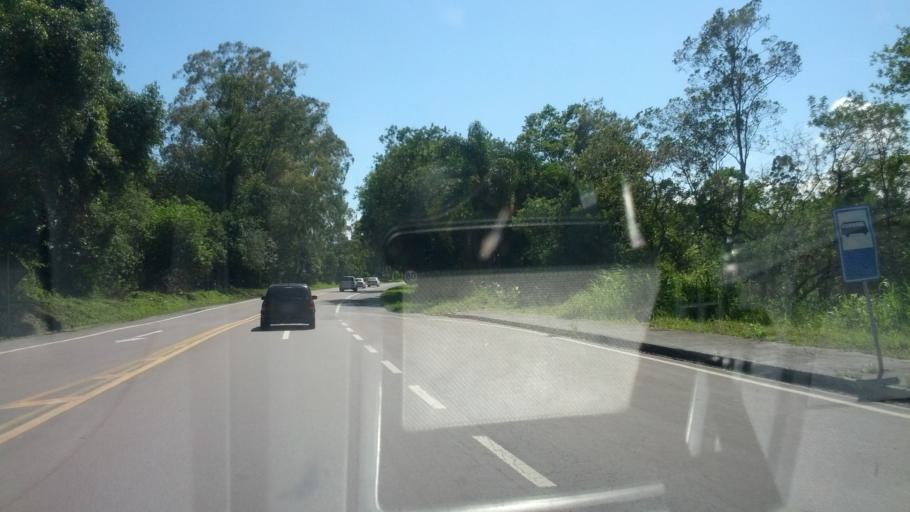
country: BR
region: Santa Catarina
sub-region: Rio Do Sul
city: Rio do Sul
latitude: -27.1745
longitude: -49.5892
